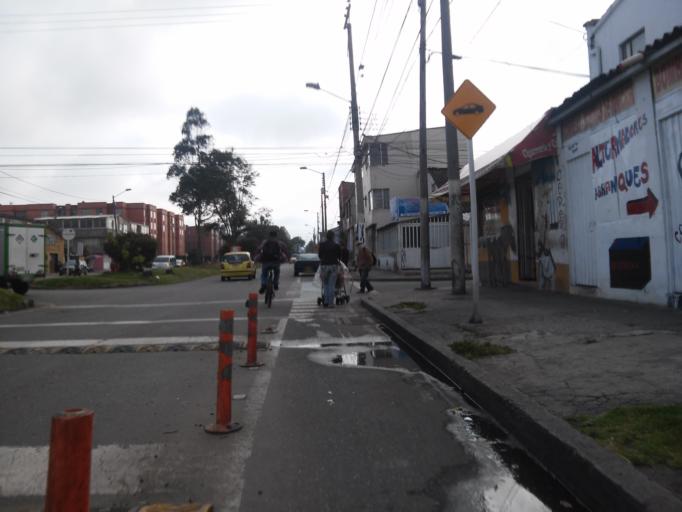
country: CO
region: Bogota D.C.
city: Bogota
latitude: 4.6159
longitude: -74.1486
